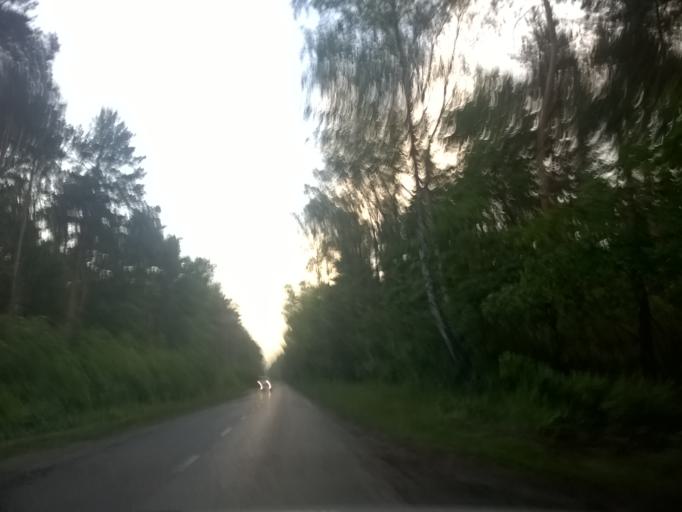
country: PL
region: Masovian Voivodeship
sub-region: Powiat piaseczynski
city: Konstancin-Jeziorna
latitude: 52.0688
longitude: 21.1162
